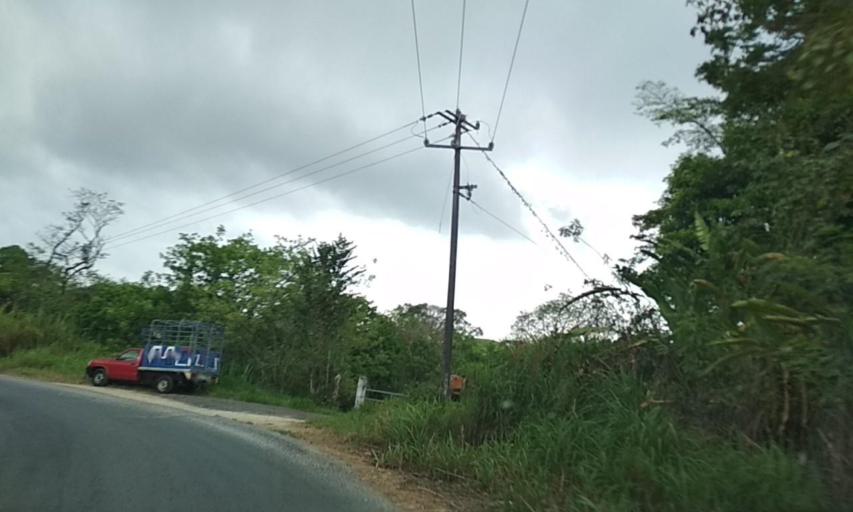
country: MX
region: Tabasco
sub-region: Huimanguillo
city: Francisco Rueda
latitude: 17.6314
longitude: -94.0897
